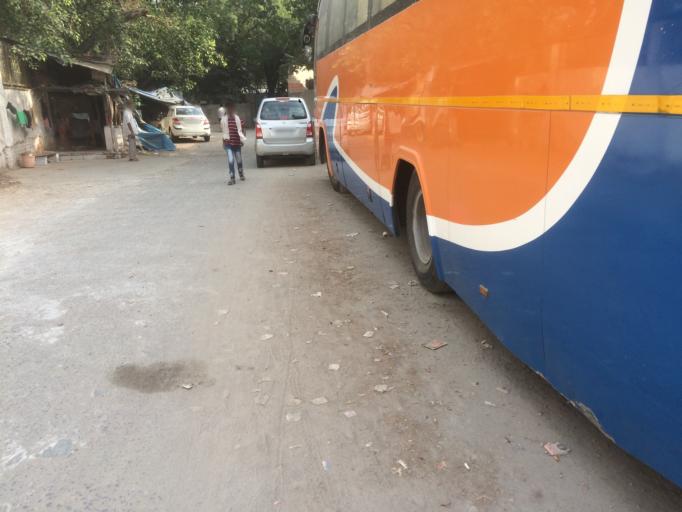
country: IN
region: NCT
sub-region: New Delhi
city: New Delhi
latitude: 28.5811
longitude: 77.1884
